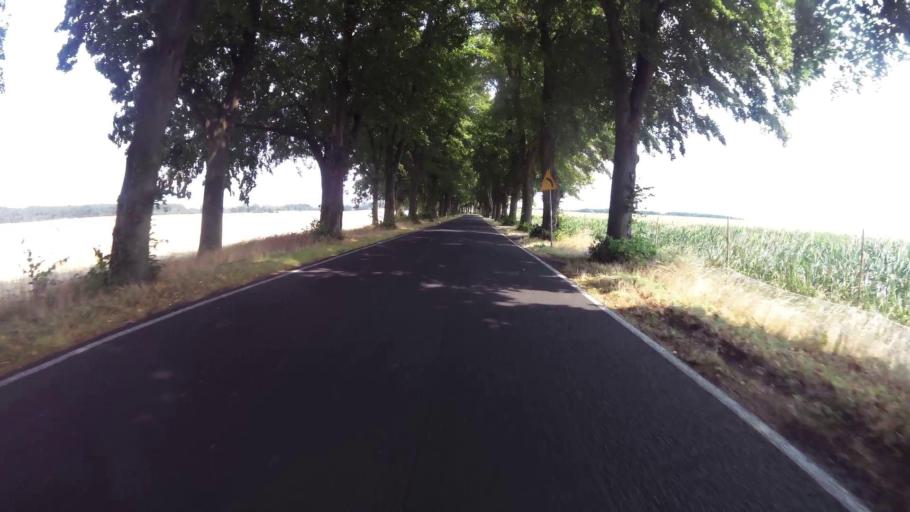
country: PL
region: West Pomeranian Voivodeship
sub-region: Powiat gryfinski
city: Mieszkowice
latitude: 52.8236
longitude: 14.4773
